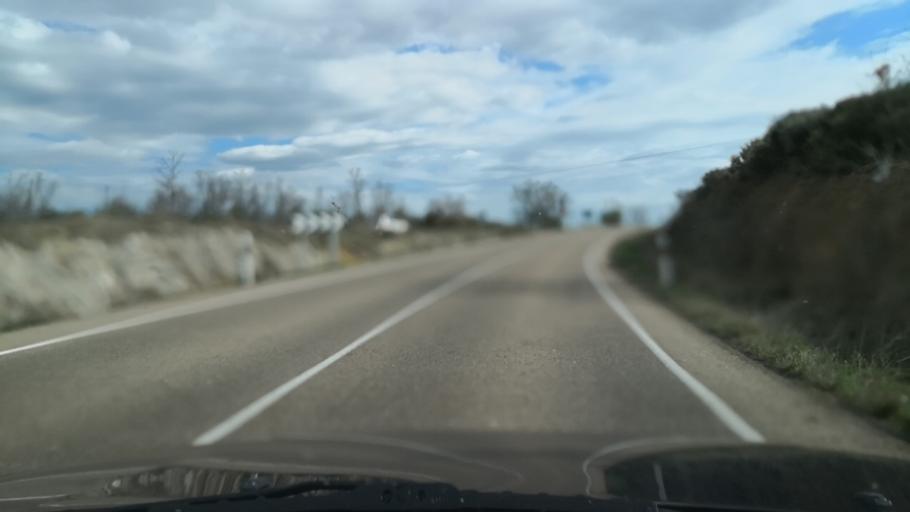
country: ES
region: Castille and Leon
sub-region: Provincia de Salamanca
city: Robleda
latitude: 40.4276
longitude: -6.5992
